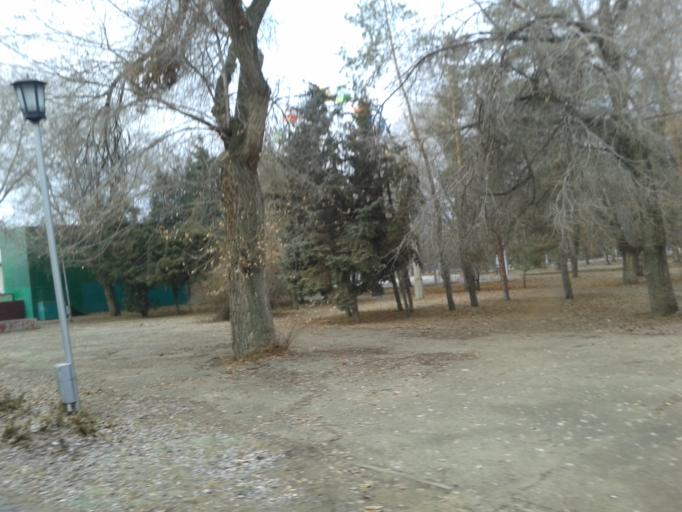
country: RU
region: Volgograd
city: Volgograd
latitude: 48.7089
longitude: 44.5095
